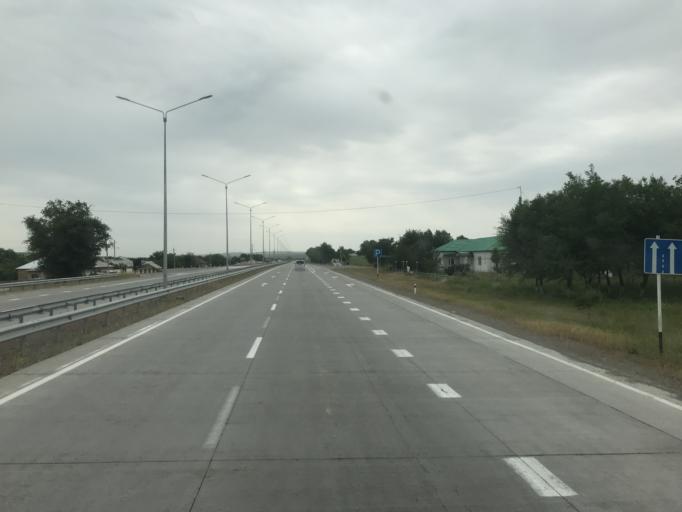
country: KZ
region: Ongtustik Qazaqstan
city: Qazyqurt
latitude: 41.8857
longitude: 69.4420
